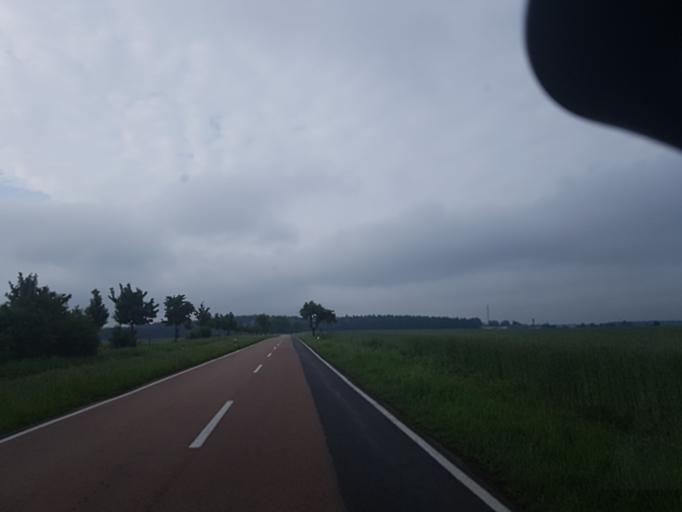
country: DE
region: Saxony-Anhalt
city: Klieken
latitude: 51.9797
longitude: 12.3486
